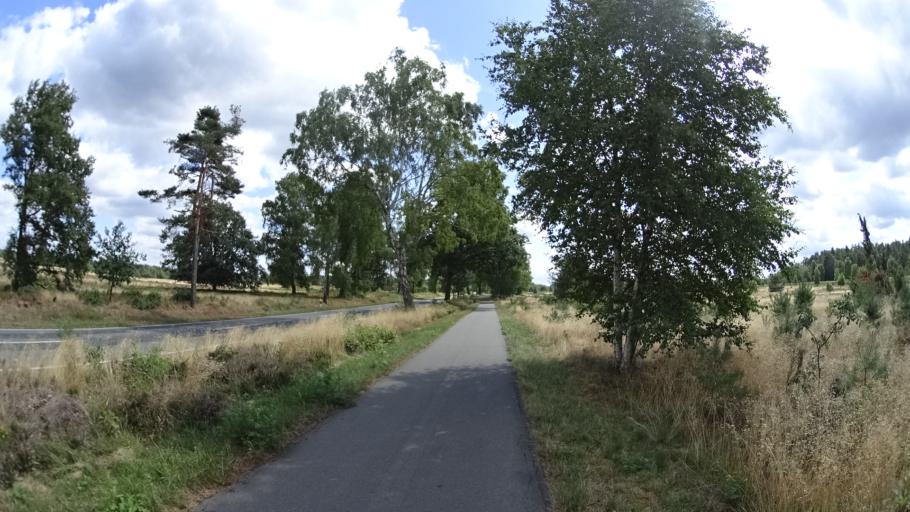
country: DE
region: Lower Saxony
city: Undeloh
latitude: 53.2183
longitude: 9.9420
